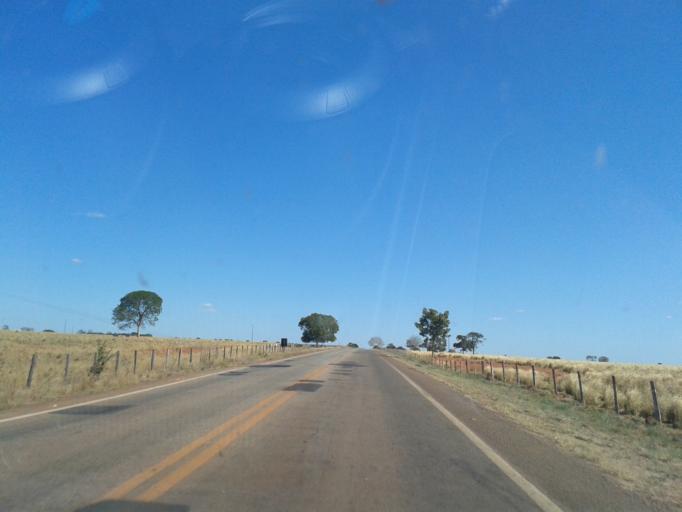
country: BR
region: Goias
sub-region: Crixas
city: Crixas
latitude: -14.1425
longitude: -50.3571
